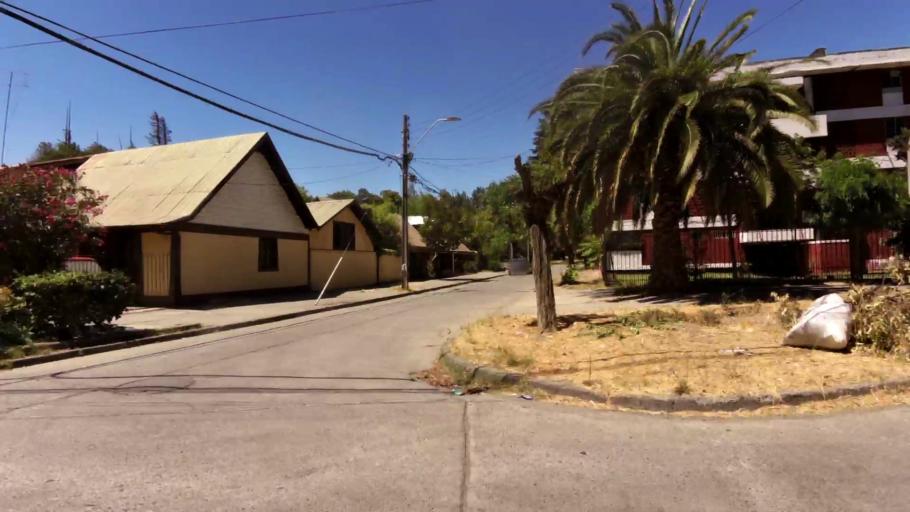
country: CL
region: O'Higgins
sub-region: Provincia de Cachapoal
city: Rancagua
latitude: -34.1670
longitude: -70.7557
